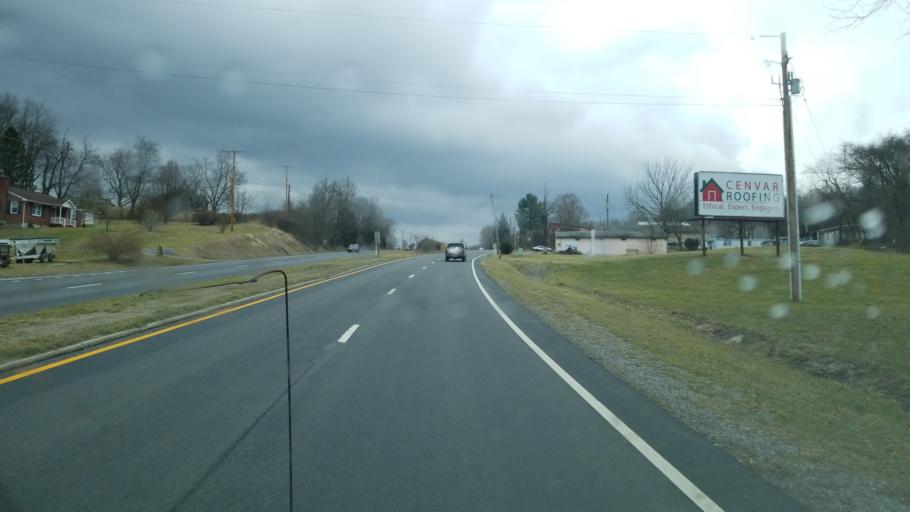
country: US
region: Virginia
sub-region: Giles County
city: Pearisburg
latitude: 37.3130
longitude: -80.7333
